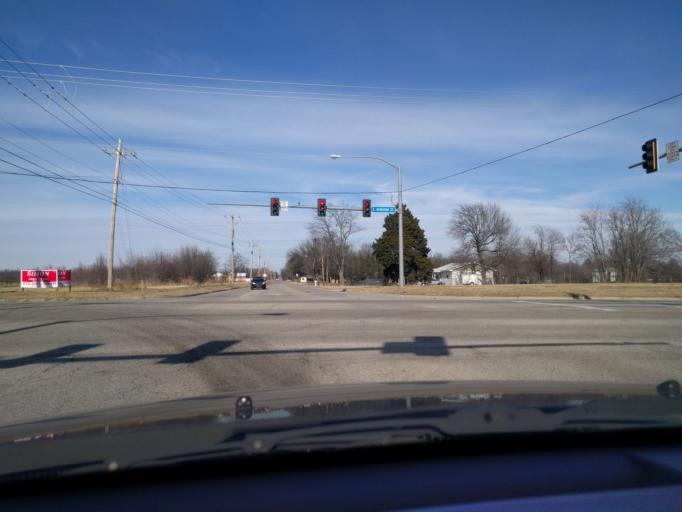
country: US
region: Oklahoma
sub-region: Tulsa County
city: Broken Arrow
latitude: 36.0607
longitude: -95.7081
